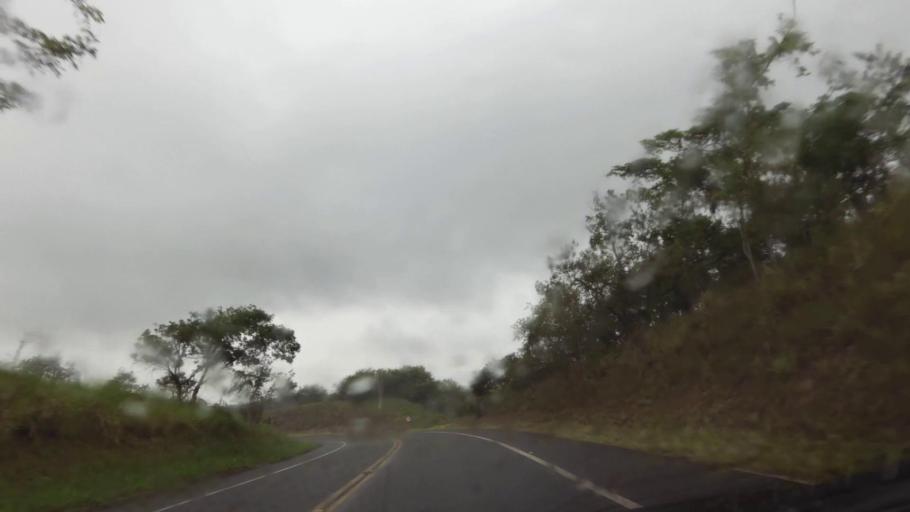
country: BR
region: Espirito Santo
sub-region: Guarapari
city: Guarapari
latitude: -20.6414
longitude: -40.5328
